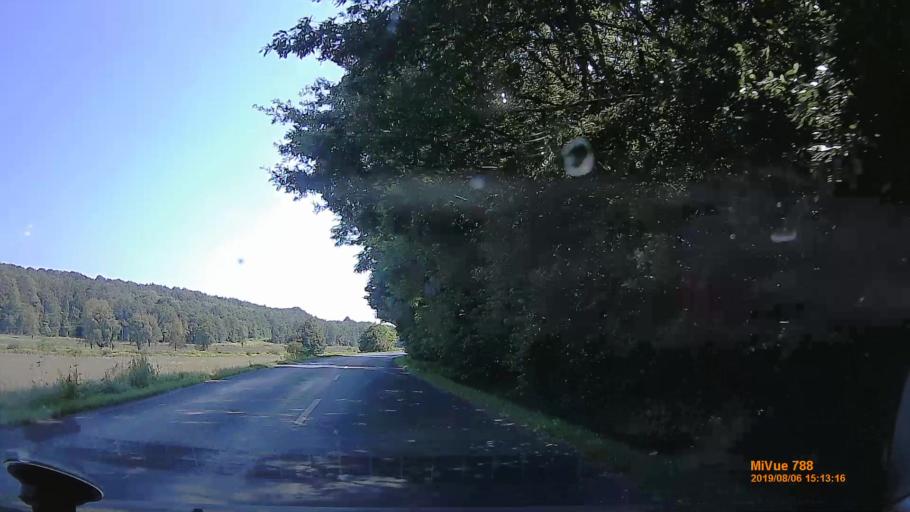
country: HU
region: Zala
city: Murakeresztur
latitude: 46.3565
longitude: 16.9777
